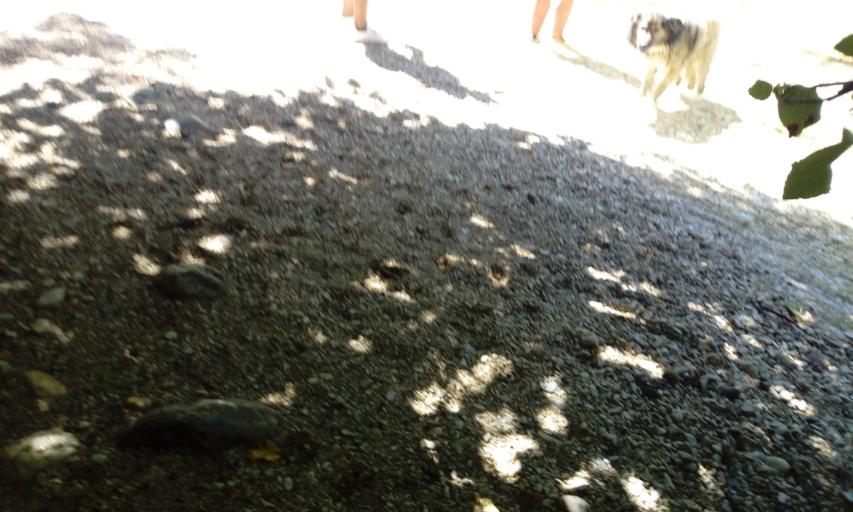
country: GR
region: Epirus
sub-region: Nomos Prevezis
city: Kanalaki
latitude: 39.3272
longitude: 20.6248
